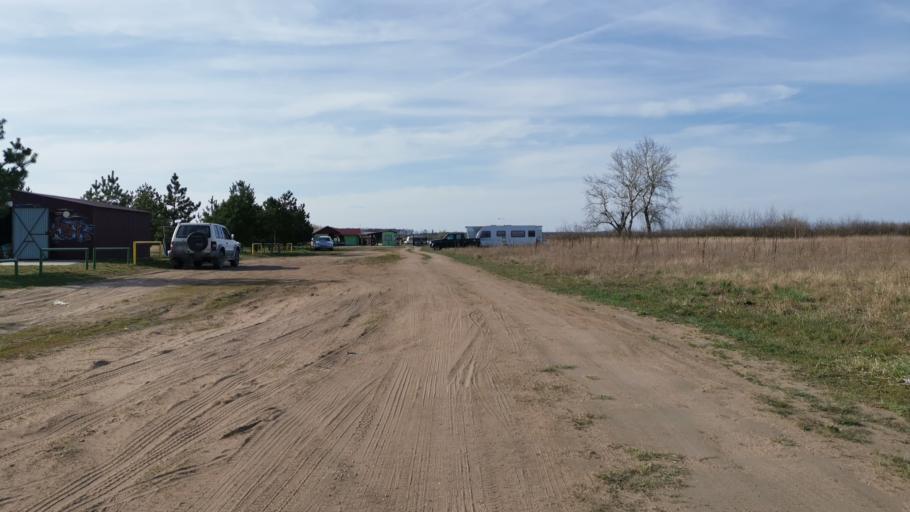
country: CZ
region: South Moravian
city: Tvrdonice
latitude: 48.7301
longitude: 17.0381
